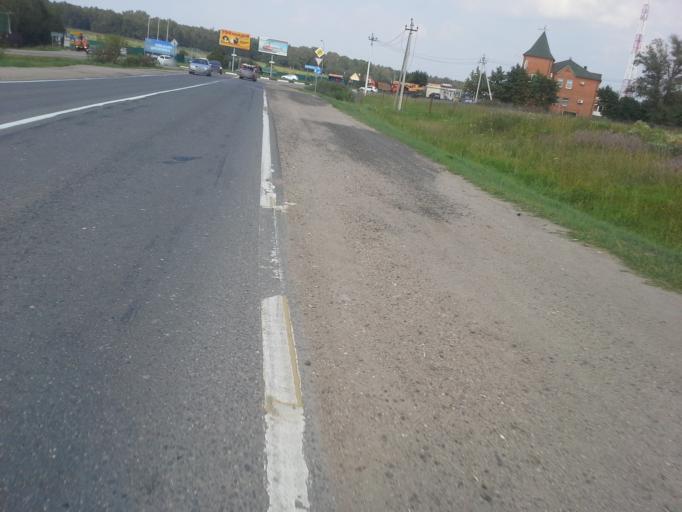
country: RU
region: Moskovskaya
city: Istra
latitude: 55.8600
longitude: 36.7959
